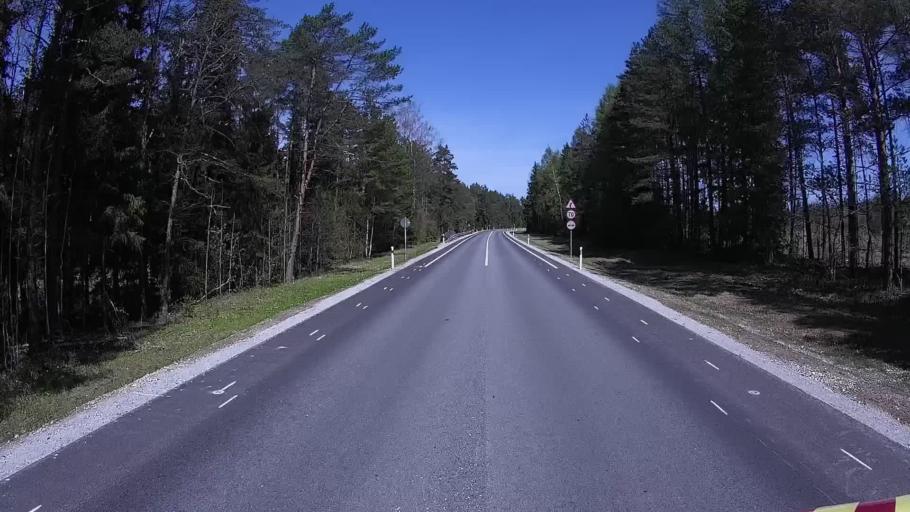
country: EE
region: Laeaene
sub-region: Ridala Parish
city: Uuemoisa
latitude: 59.0388
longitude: 23.8292
